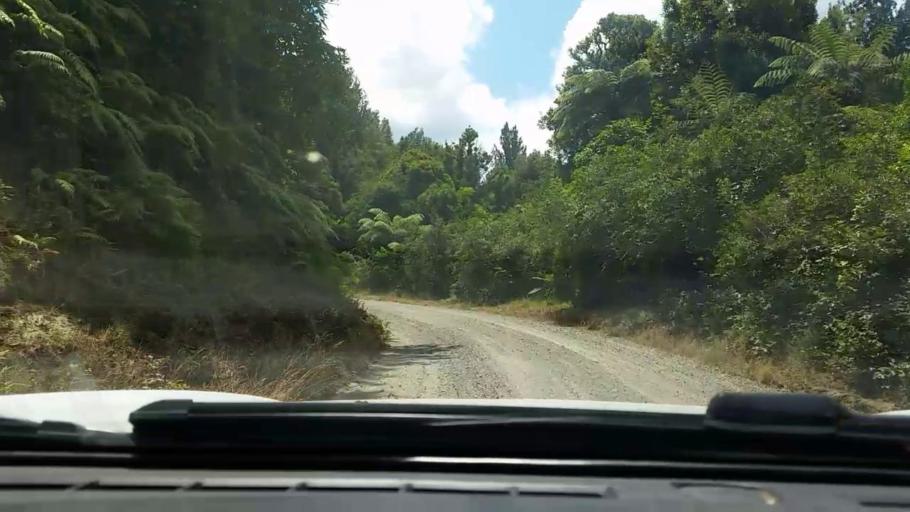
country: NZ
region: Bay of Plenty
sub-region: Kawerau District
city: Kawerau
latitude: -38.0242
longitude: 176.5664
